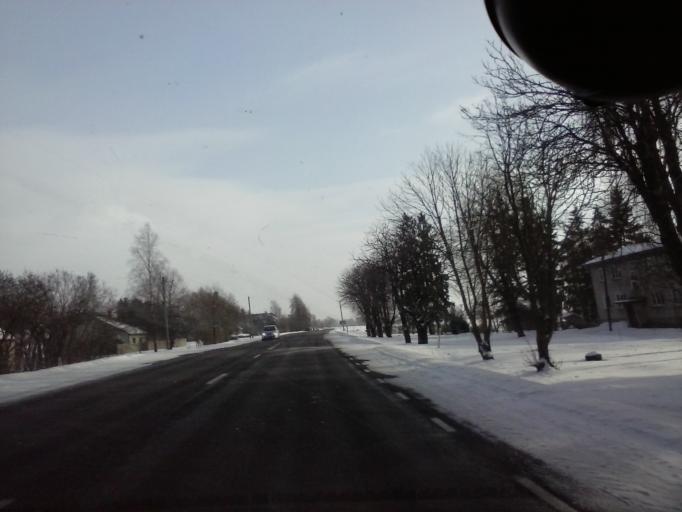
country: EE
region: Tartu
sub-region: Puhja vald
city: Puhja
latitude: 58.3372
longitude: 26.1833
